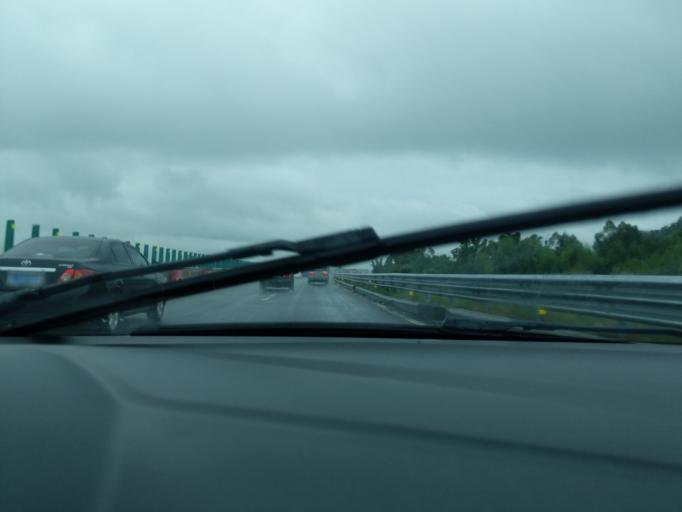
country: CN
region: Guangdong
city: Yueshan
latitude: 22.4650
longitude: 112.7030
